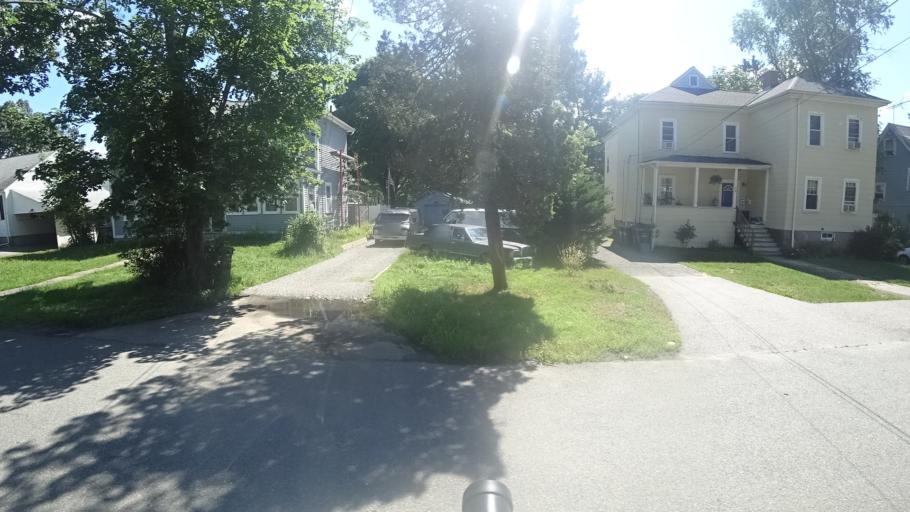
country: US
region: Massachusetts
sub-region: Norfolk County
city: Dedham
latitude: 42.2568
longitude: -71.1515
